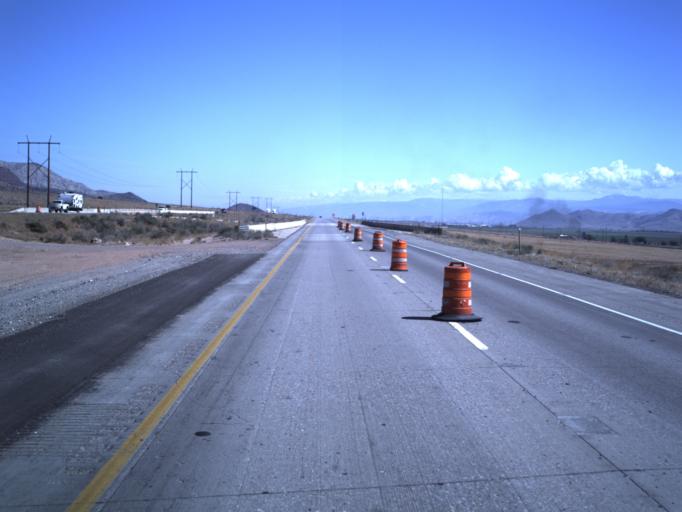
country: US
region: Utah
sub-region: Sevier County
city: Richfield
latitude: 38.8115
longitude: -112.0560
